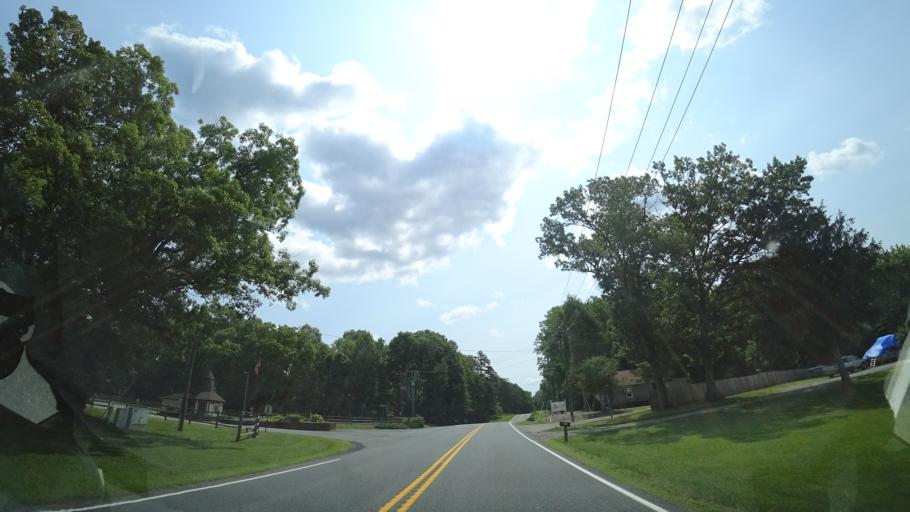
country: US
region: Virginia
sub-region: Louisa County
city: Louisa
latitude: 38.0835
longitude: -77.8390
